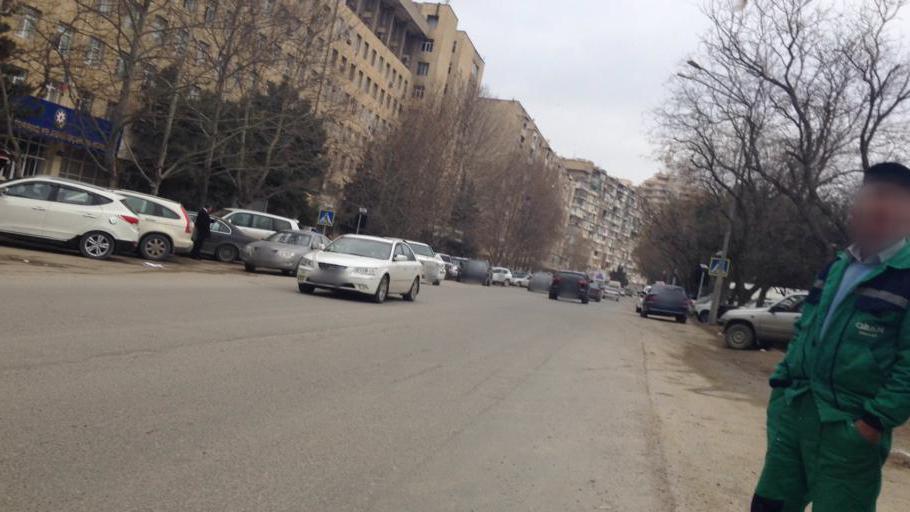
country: AZ
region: Baki
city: Badamdar
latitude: 40.3890
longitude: 49.8156
